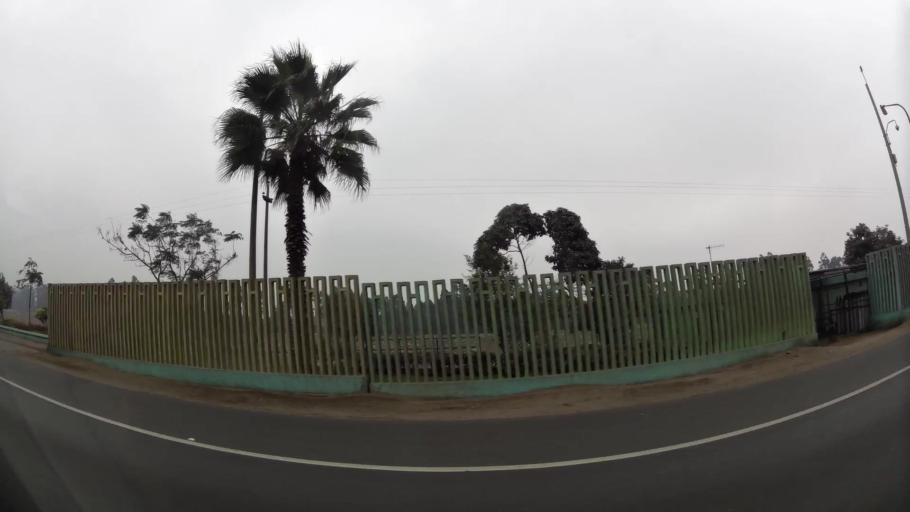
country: PE
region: Lima
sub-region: Lima
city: Vitarte
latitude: -12.0201
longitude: -76.9510
